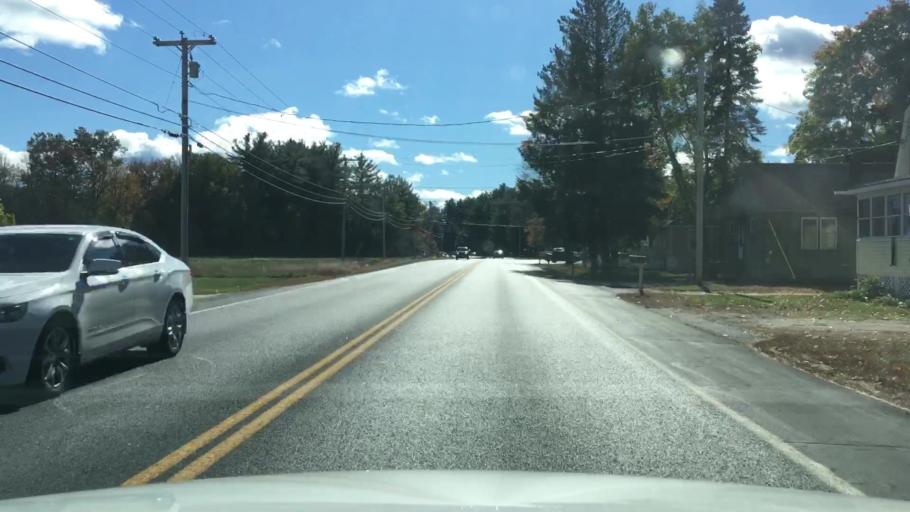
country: US
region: Maine
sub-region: York County
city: South Sanford
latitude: 43.4363
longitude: -70.7331
